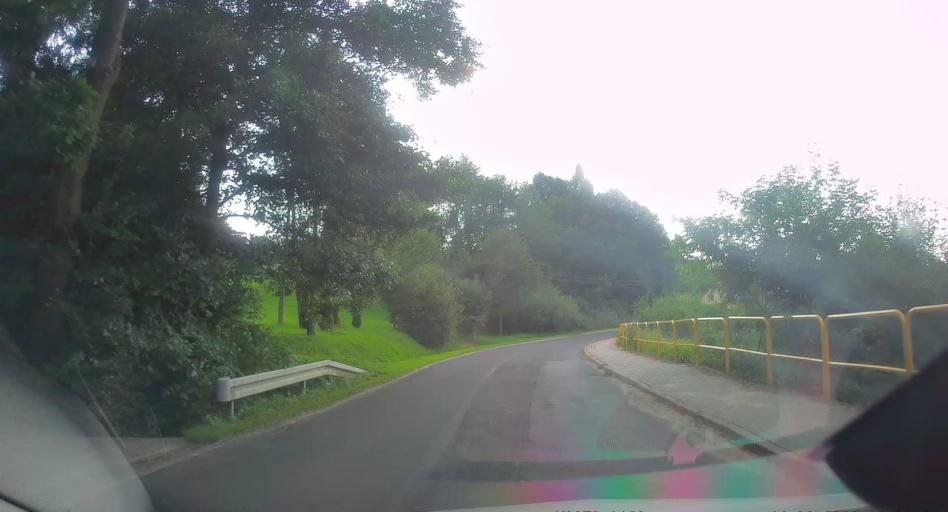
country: PL
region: Subcarpathian Voivodeship
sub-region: Powiat debicki
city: Debica
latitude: 49.9939
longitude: 21.4229
